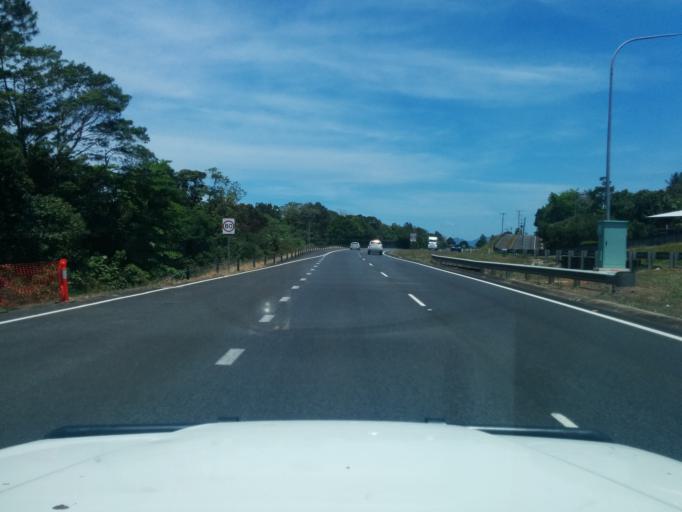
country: AU
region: Queensland
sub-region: Cairns
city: Redlynch
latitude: -16.9099
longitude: 145.7144
